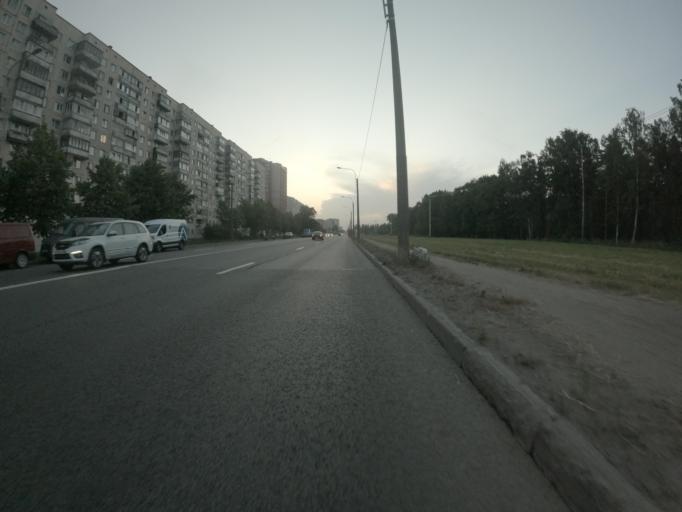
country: RU
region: St.-Petersburg
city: Krasnogvargeisky
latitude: 59.9473
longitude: 30.5041
